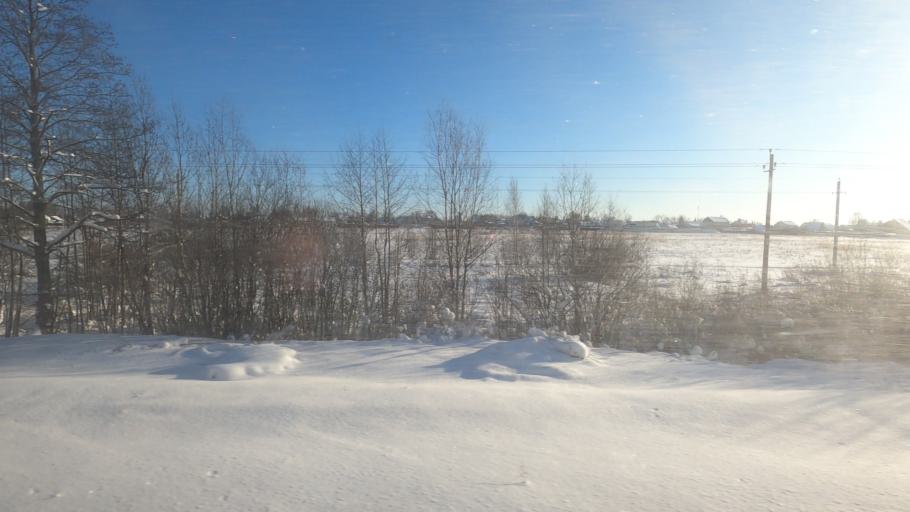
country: RU
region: Moskovskaya
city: Orud'yevo
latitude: 56.4397
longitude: 37.5108
